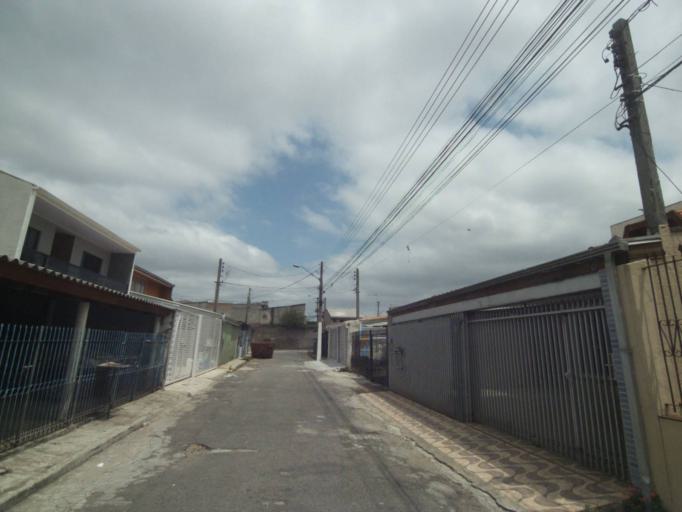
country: BR
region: Parana
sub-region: Sao Jose Dos Pinhais
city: Sao Jose dos Pinhais
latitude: -25.5383
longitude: -49.2694
